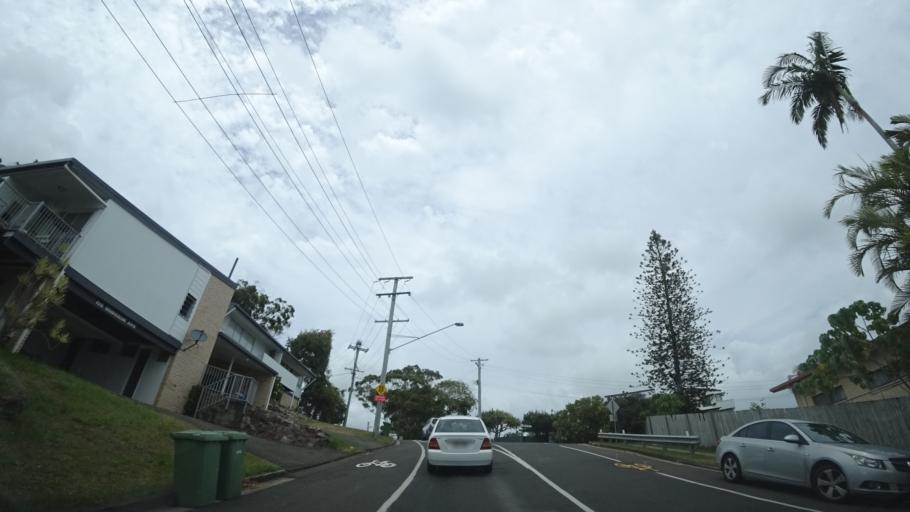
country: AU
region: Queensland
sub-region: Sunshine Coast
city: Mooloolaba
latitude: -26.6731
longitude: 153.1040
